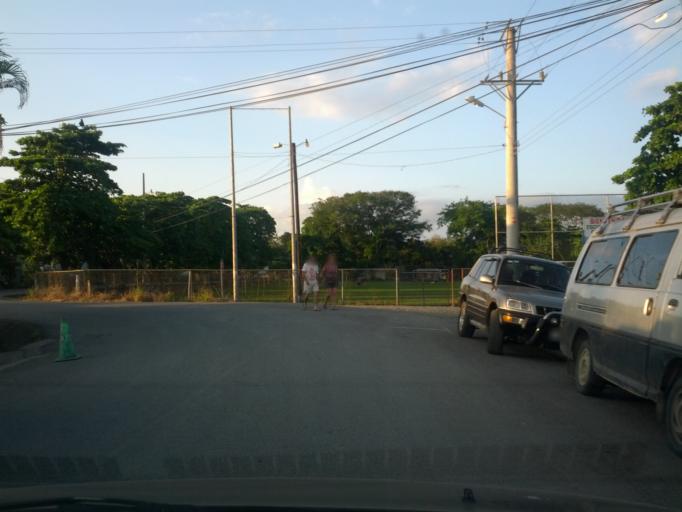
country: CR
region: Puntarenas
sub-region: Canton de Golfito
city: Golfito
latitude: 8.5383
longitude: -83.3063
